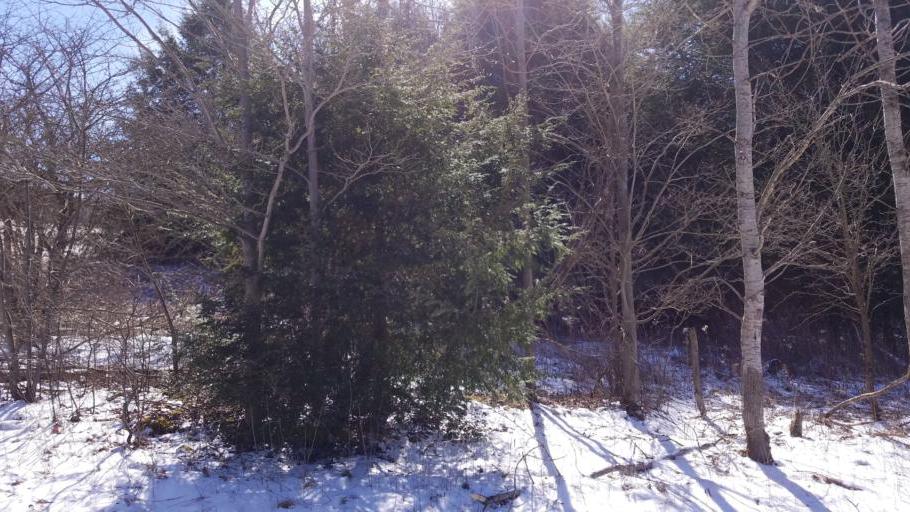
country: US
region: New York
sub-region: Allegany County
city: Andover
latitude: 41.9592
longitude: -77.7405
